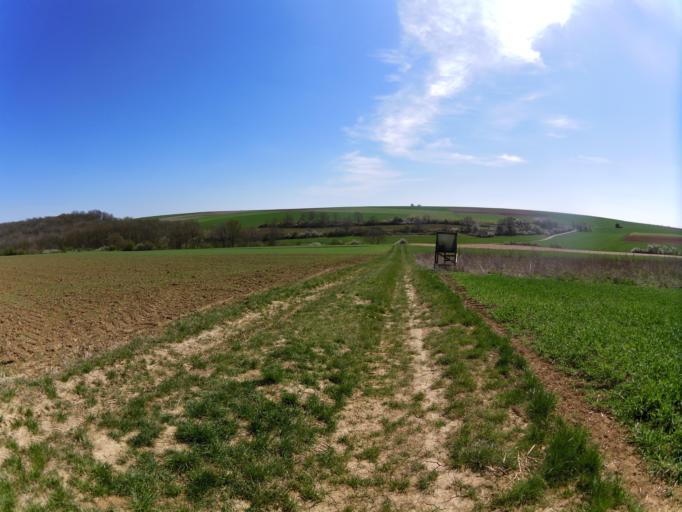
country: DE
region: Bavaria
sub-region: Regierungsbezirk Unterfranken
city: Winterhausen
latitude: 49.6941
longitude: 9.9932
